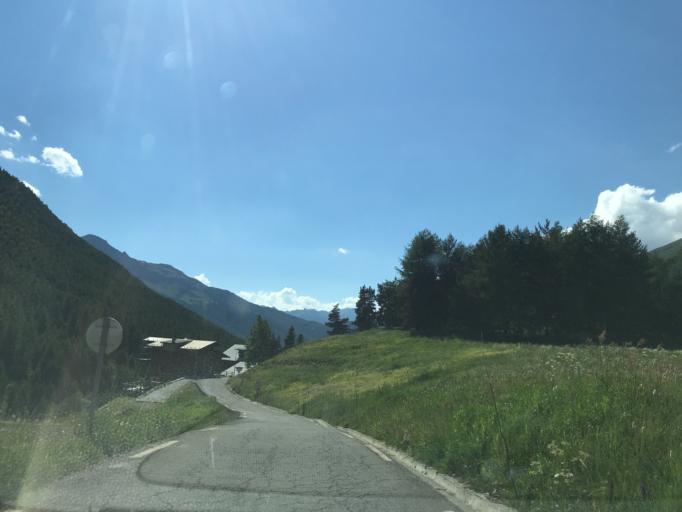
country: IT
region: Piedmont
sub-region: Provincia di Cuneo
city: Pontechianale
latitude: 44.7211
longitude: 6.8910
